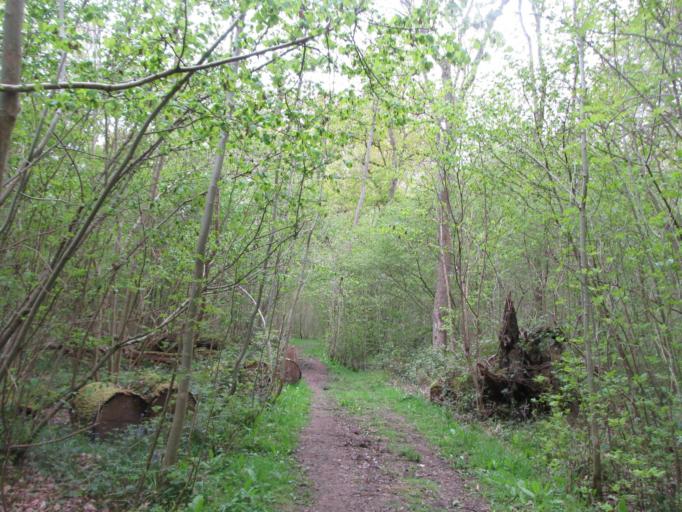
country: GB
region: England
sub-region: Royal Borough of Windsor and Maidenhead
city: Bisham
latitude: 51.5457
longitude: -0.7696
